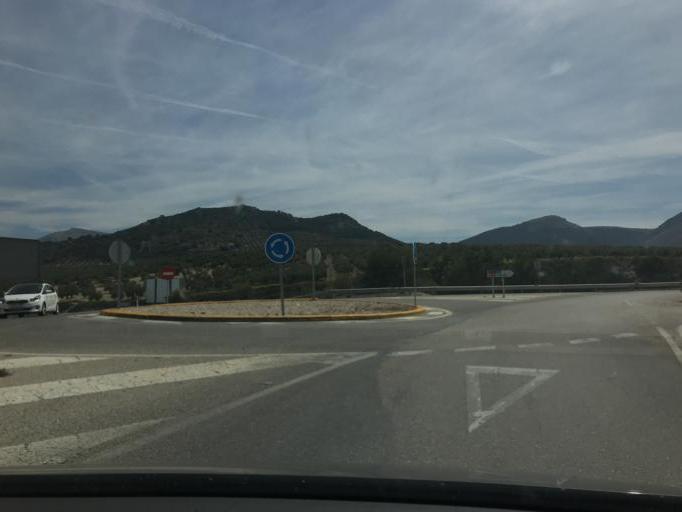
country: ES
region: Andalusia
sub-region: Provincia de Jaen
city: Jamilena
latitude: 37.7629
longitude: -3.9194
